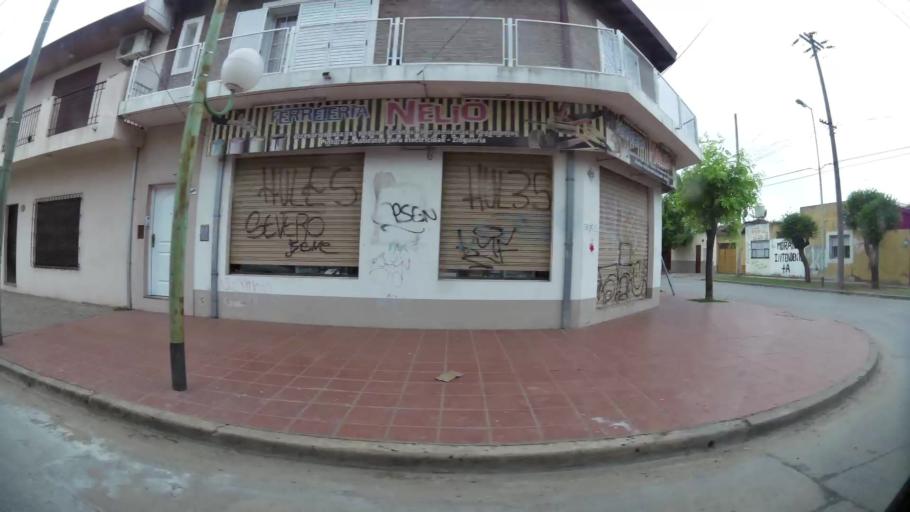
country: AR
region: Buenos Aires
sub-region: Partido de Zarate
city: Zarate
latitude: -34.1095
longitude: -59.0248
